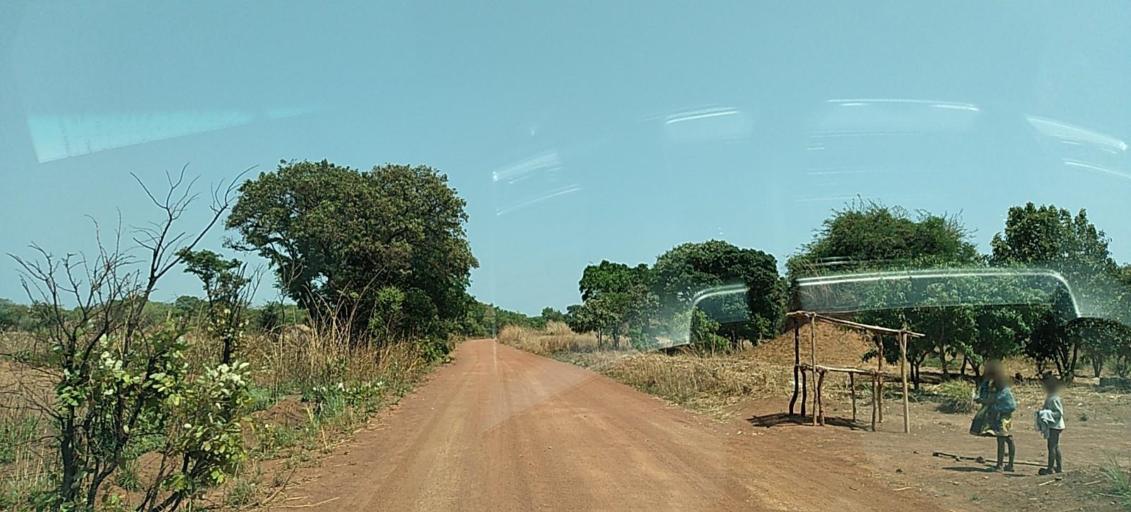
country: ZM
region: Copperbelt
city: Chingola
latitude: -12.5348
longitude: 27.7241
